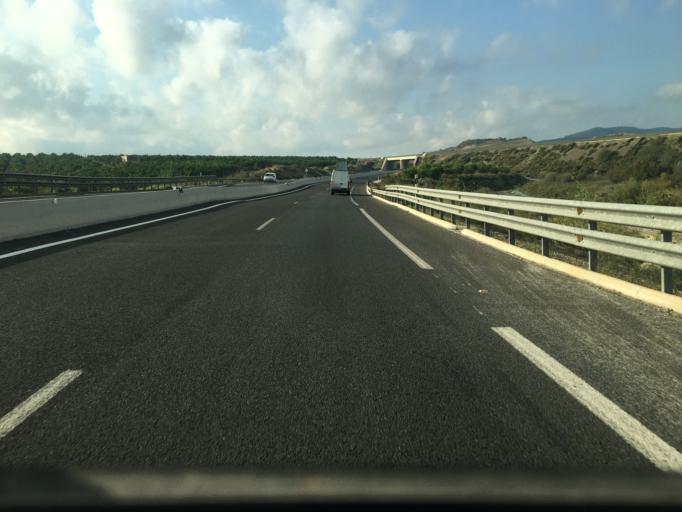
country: ES
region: Murcia
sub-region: Murcia
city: Beniel
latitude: 37.9910
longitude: -0.9753
